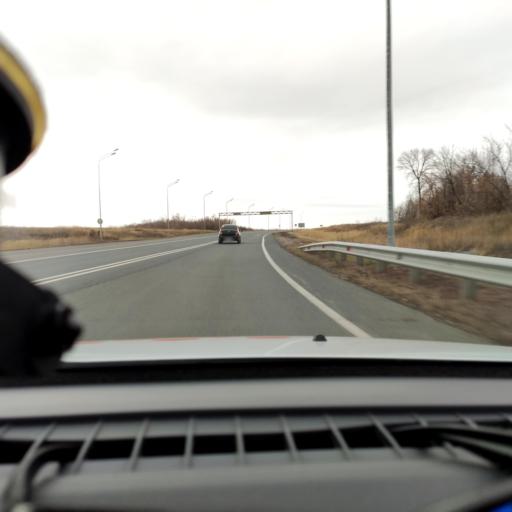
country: RU
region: Samara
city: Smyshlyayevka
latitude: 53.1455
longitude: 50.3910
